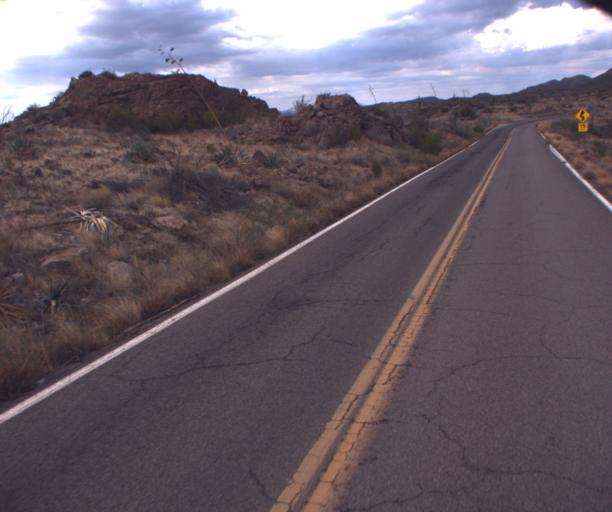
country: US
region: Arizona
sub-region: Pinal County
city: Gold Camp
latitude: 33.5387
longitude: -111.3264
